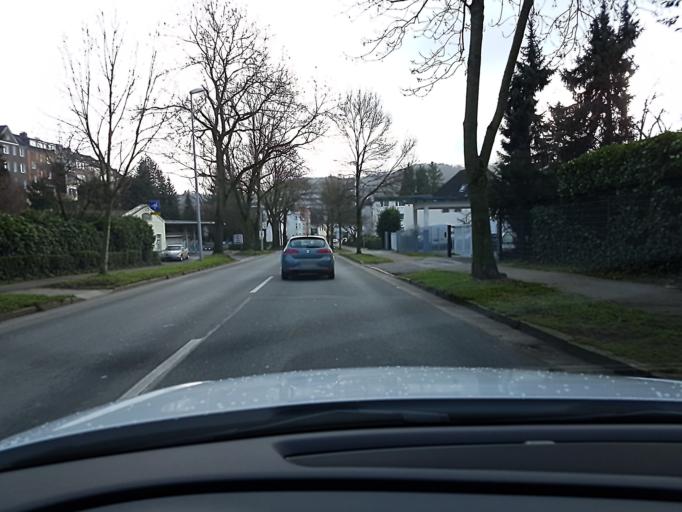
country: DE
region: North Rhine-Westphalia
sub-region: Regierungsbezirk Dusseldorf
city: Heiligenhaus
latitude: 51.3641
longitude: 6.9451
